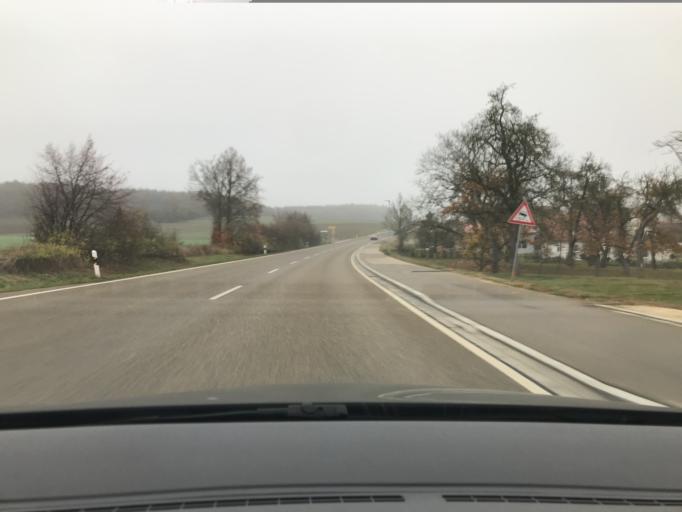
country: DE
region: Bavaria
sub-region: Swabia
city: Fremdingen
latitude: 48.9423
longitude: 10.4592
